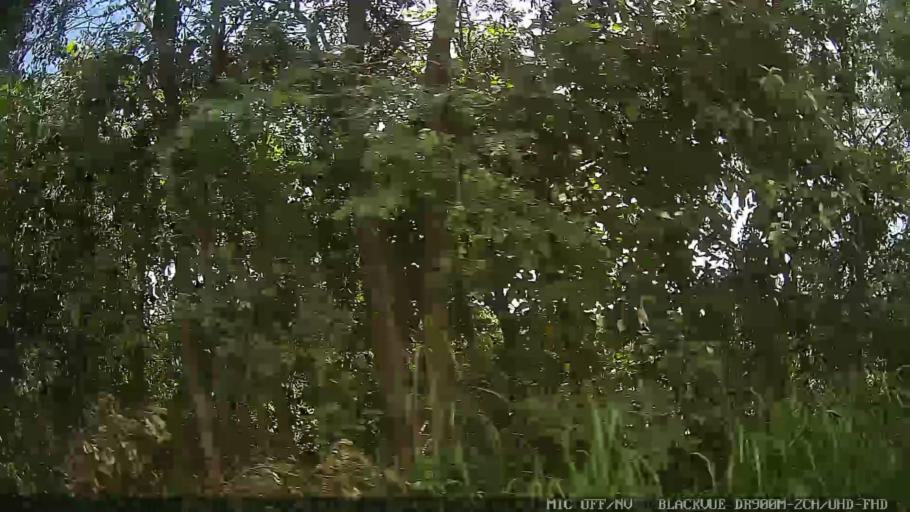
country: BR
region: Sao Paulo
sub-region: Atibaia
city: Atibaia
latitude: -23.0698
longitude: -46.6222
